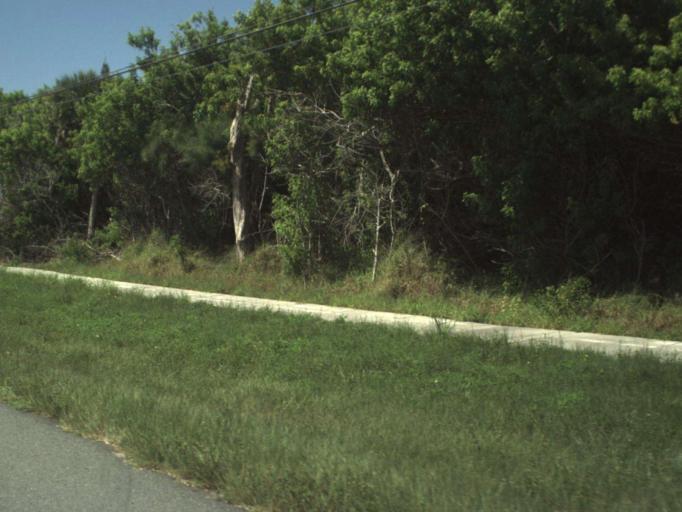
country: US
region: Florida
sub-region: Saint Lucie County
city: Fort Pierce North
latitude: 27.5174
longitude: -80.3093
